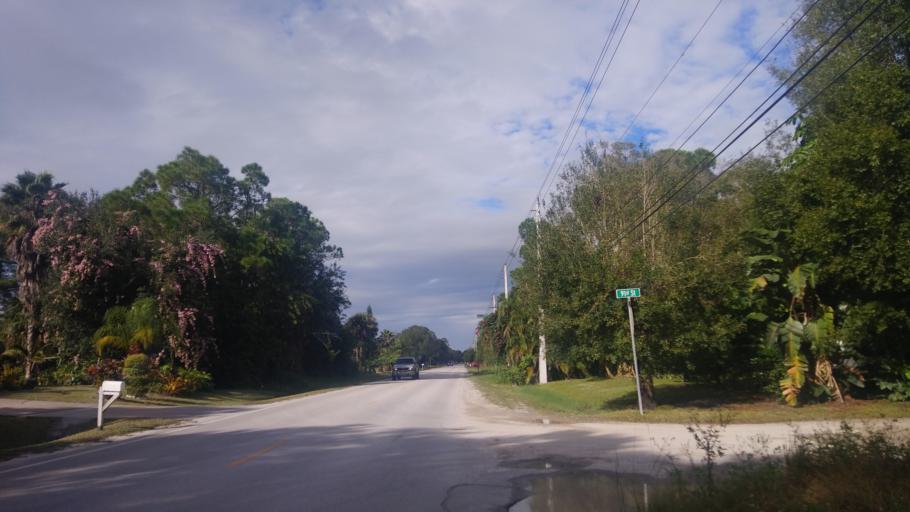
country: US
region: Florida
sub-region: Indian River County
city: Fellsmere
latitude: 27.7614
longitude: -80.5932
